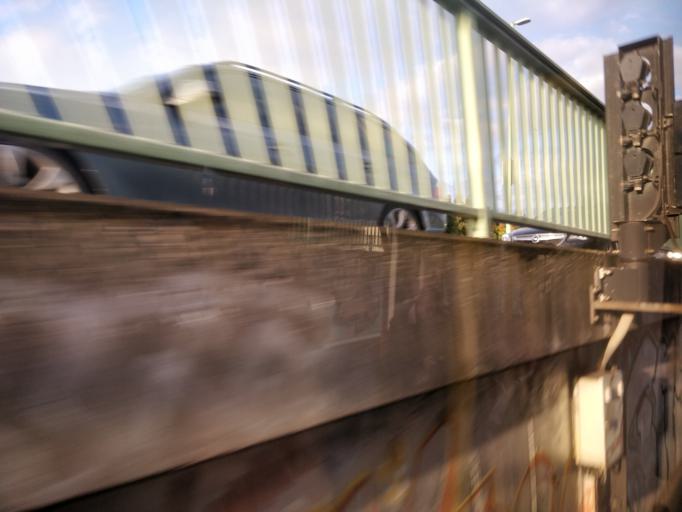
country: DE
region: North Rhine-Westphalia
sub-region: Regierungsbezirk Koln
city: Muelheim
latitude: 50.9625
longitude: 7.0011
